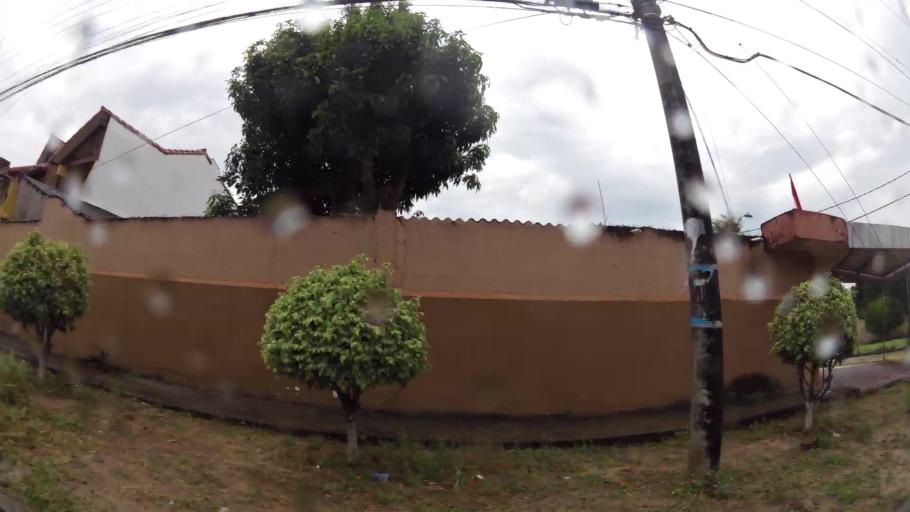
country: BO
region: Santa Cruz
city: Santa Cruz de la Sierra
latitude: -17.8014
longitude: -63.1589
